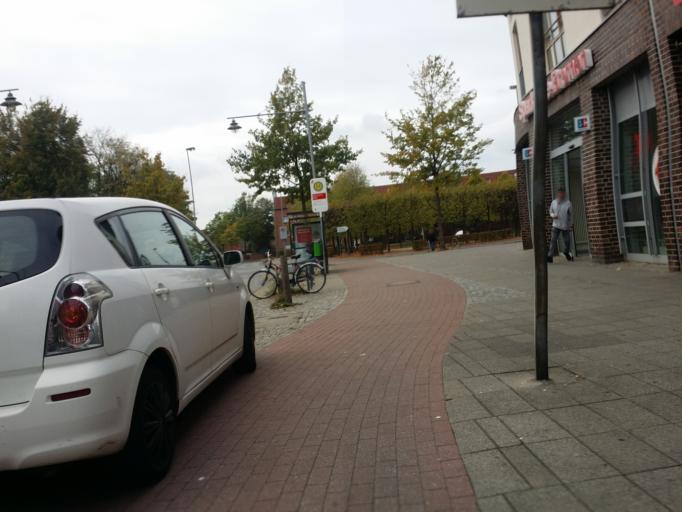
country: DE
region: Bremen
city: Bremen
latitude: 53.0343
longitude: 8.8268
